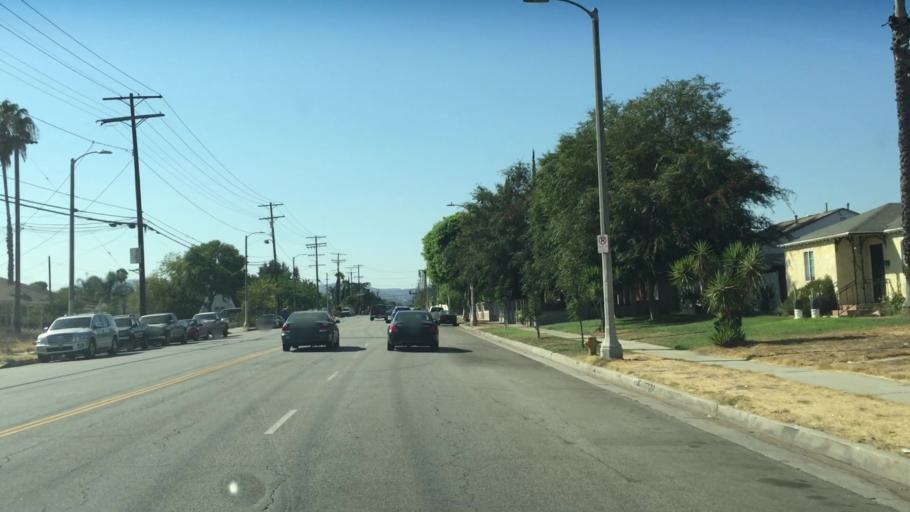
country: US
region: California
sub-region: Los Angeles County
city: San Fernando
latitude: 34.2463
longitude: -118.4304
